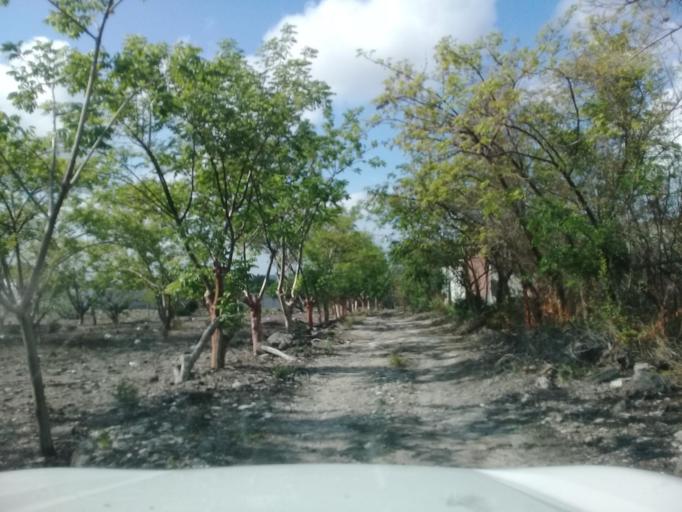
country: MX
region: Veracruz
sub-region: Emiliano Zapata
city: Plan del Rio
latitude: 19.4101
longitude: -96.6513
